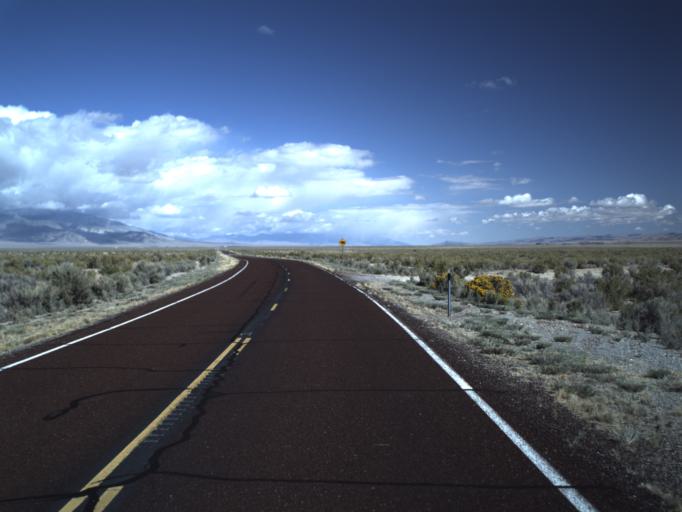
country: US
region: Nevada
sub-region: White Pine County
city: McGill
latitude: 38.9451
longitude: -114.0332
